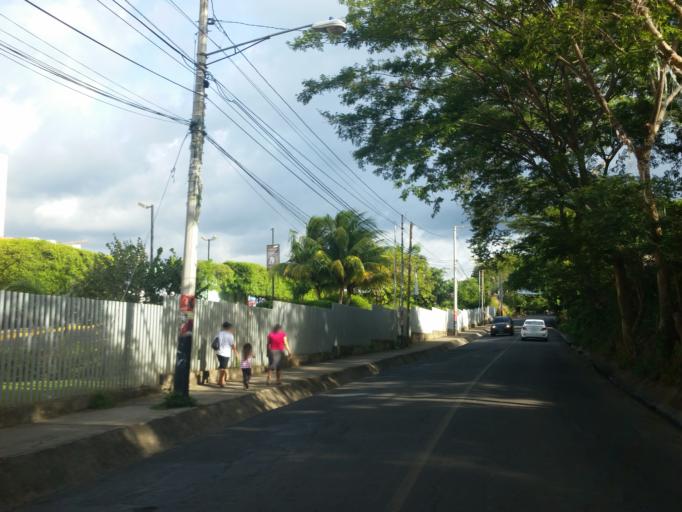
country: NI
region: Managua
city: Managua
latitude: 12.1031
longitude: -86.2502
